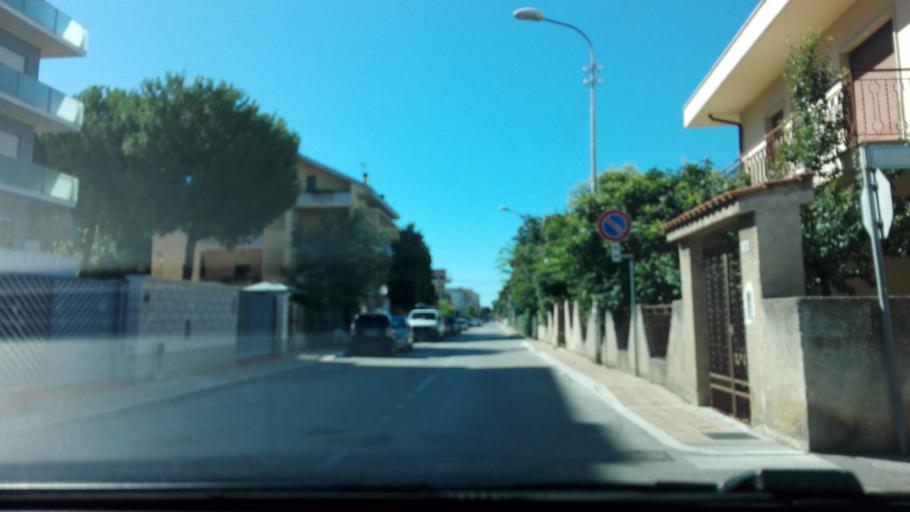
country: IT
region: Abruzzo
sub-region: Provincia di Pescara
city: Montesilvano Marina
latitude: 42.5056
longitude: 14.1691
